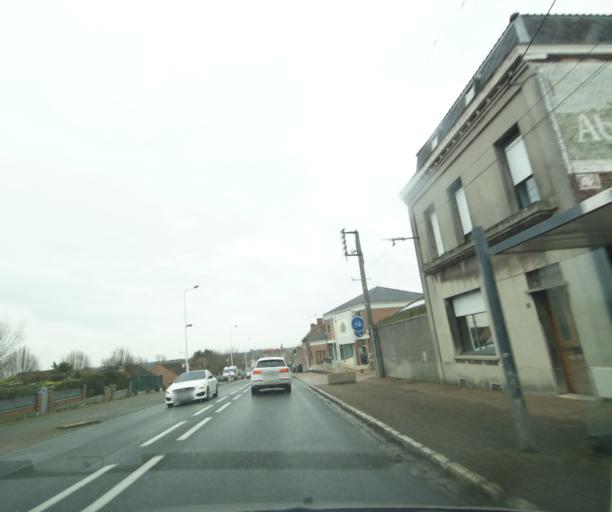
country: FR
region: Nord-Pas-de-Calais
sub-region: Departement du Nord
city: Haulchin
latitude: 50.3274
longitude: 3.4419
